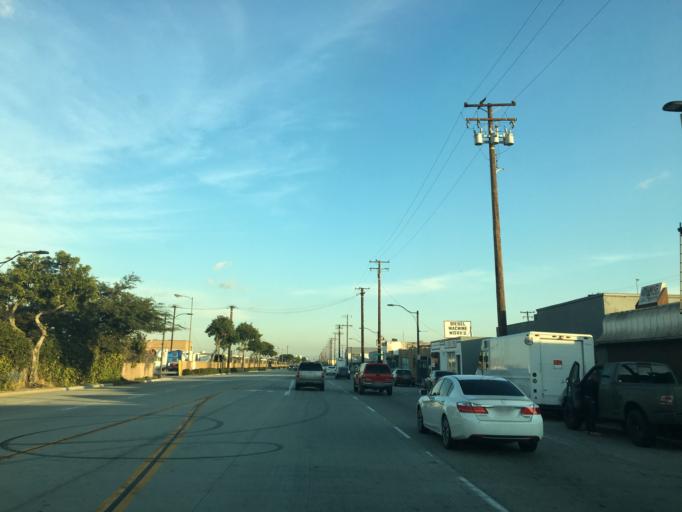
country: US
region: California
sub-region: Los Angeles County
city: East Los Angeles
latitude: 34.0084
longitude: -118.1839
